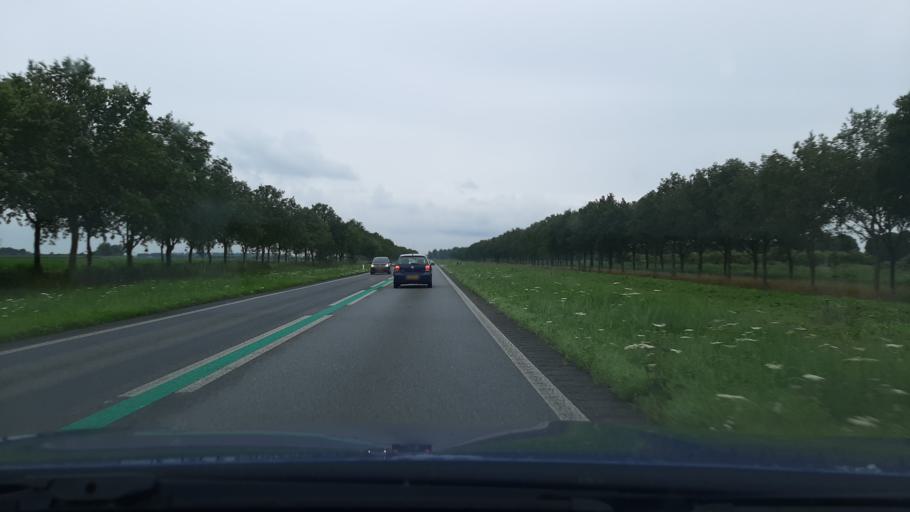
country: NL
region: Utrecht
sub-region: Gemeente Bunschoten
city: Spakenburg
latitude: 52.3119
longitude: 5.3702
